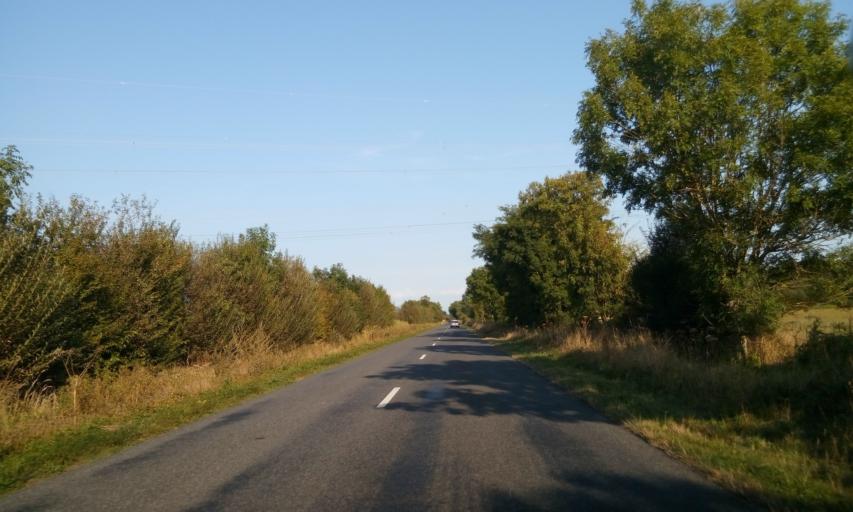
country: FR
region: Rhone-Alpes
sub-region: Departement de l'Ain
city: Amberieux-en-Dombes
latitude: 45.9981
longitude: 4.9244
